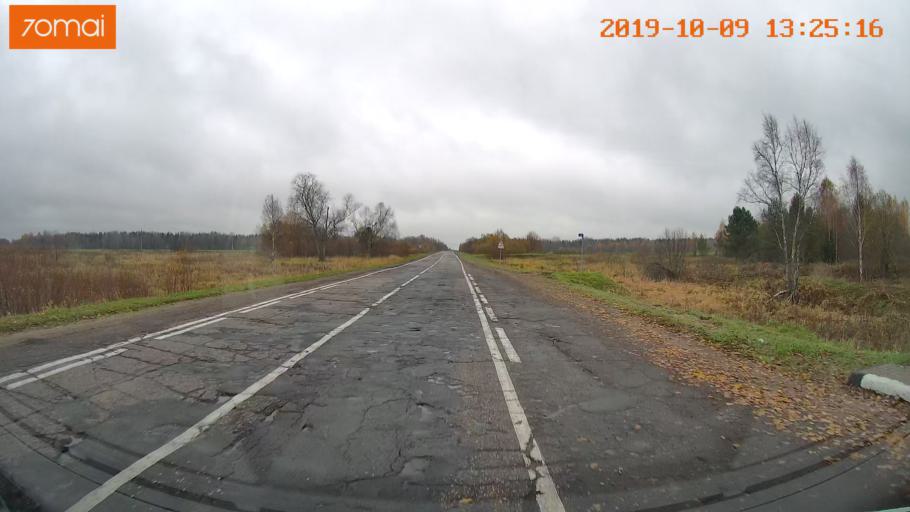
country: RU
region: Jaroslavl
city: Lyubim
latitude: 58.3294
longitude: 40.9086
